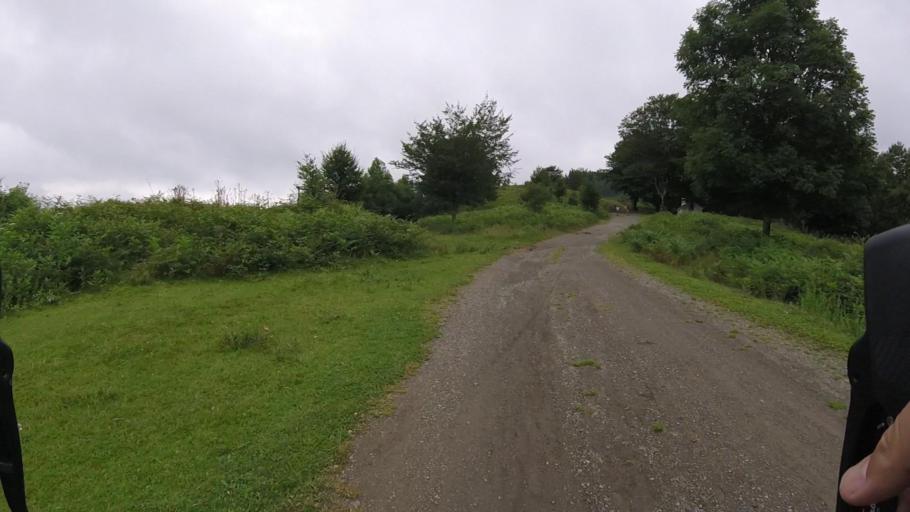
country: ES
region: Navarre
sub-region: Provincia de Navarra
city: Arano
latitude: 43.2510
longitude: -1.8908
